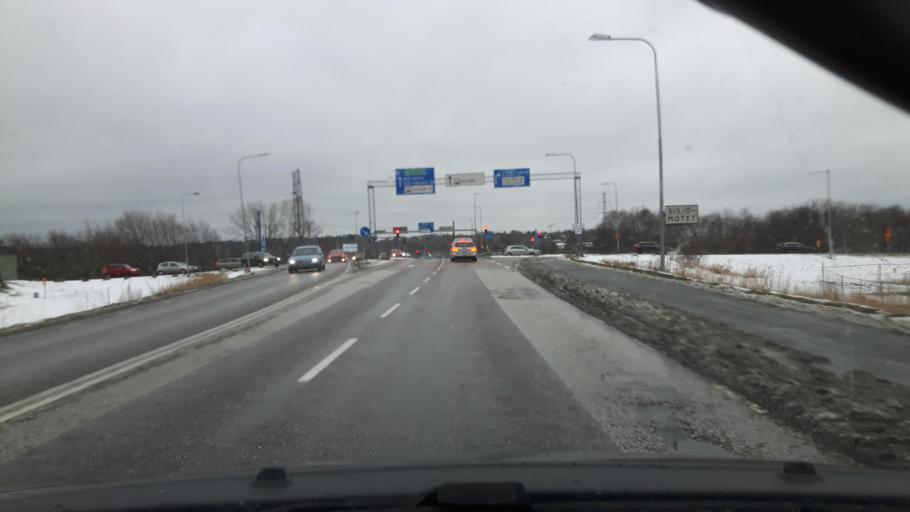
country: SE
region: Vaestra Goetaland
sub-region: Goteborg
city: Majorna
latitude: 57.6473
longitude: 11.9518
